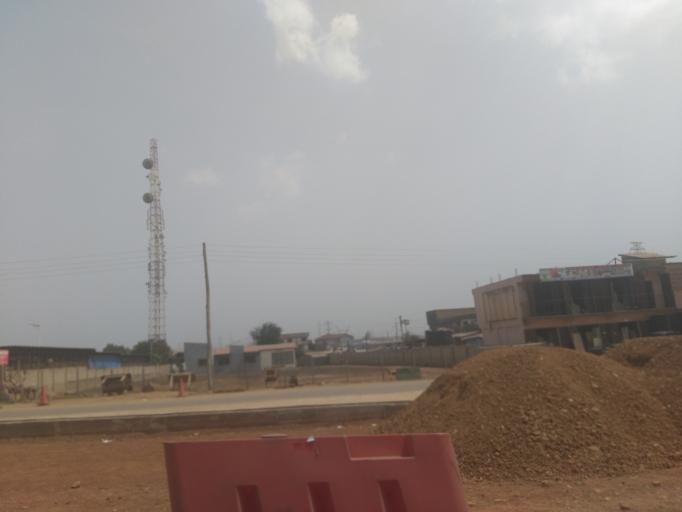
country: GH
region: Greater Accra
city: Tema
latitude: 5.6924
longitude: -0.0133
